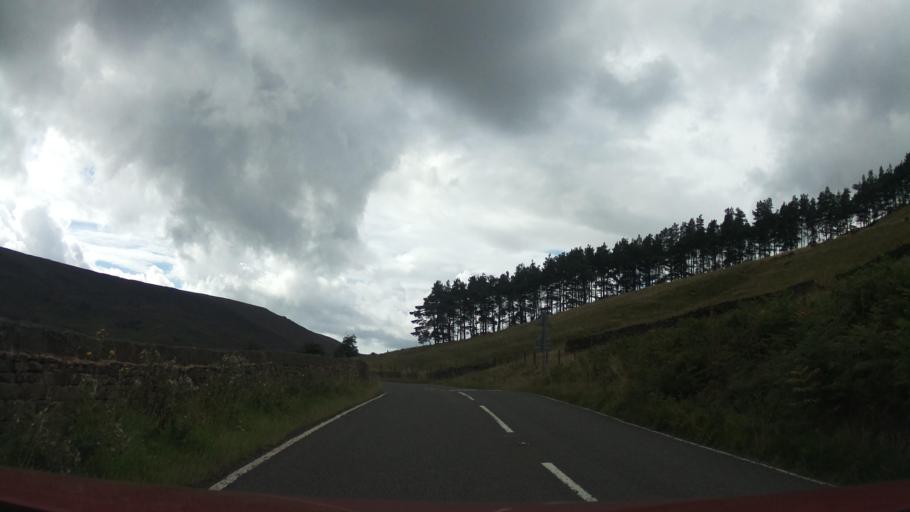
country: GB
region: England
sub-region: Kirklees
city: Meltham
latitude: 53.4989
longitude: -1.8620
